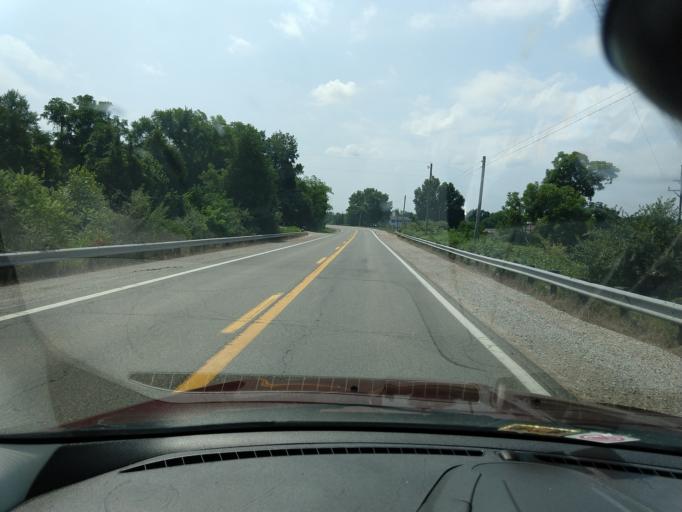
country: US
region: West Virginia
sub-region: Jackson County
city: Ravenswood
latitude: 38.8730
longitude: -81.8258
